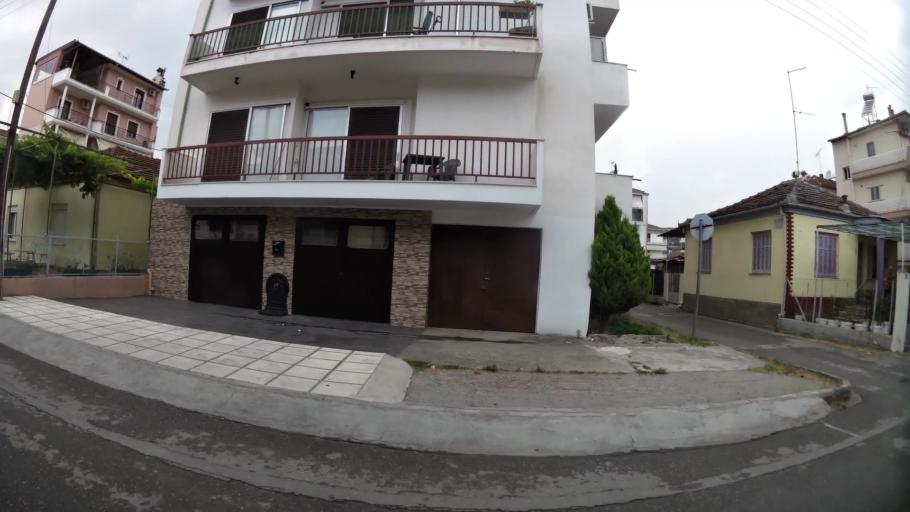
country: GR
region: Central Macedonia
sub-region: Nomos Imathias
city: Veroia
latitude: 40.5296
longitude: 22.1971
